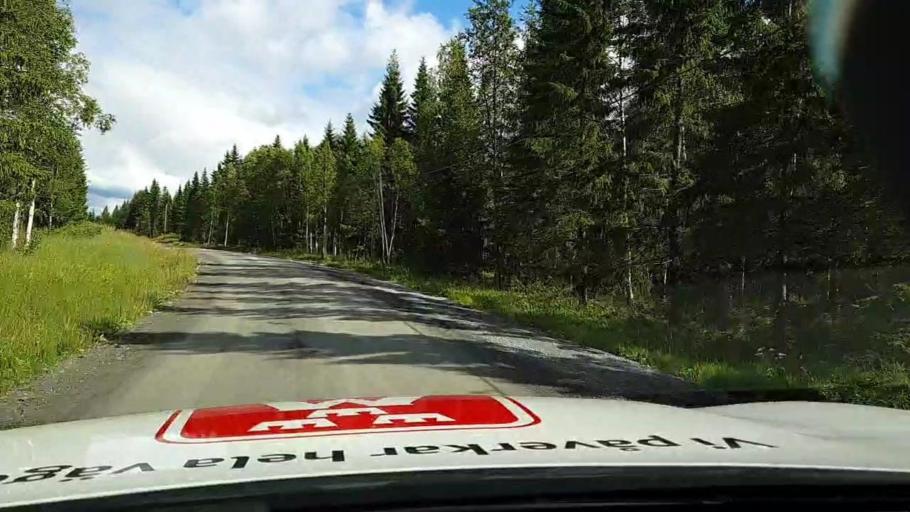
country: SE
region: Jaemtland
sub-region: Krokoms Kommun
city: Valla
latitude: 63.7067
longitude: 13.5627
